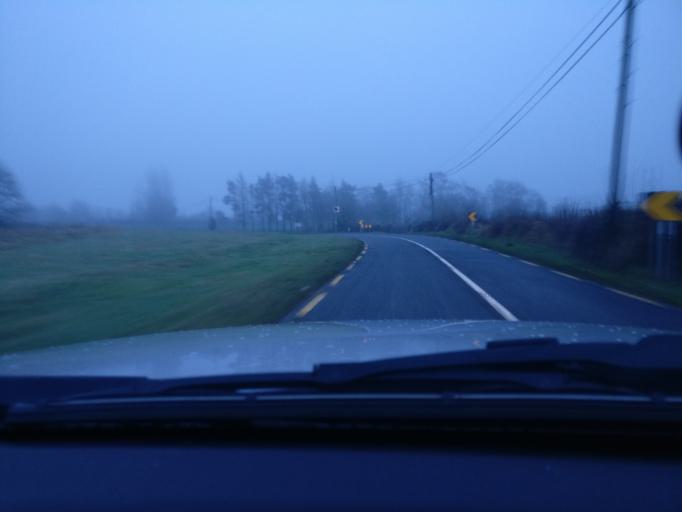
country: IE
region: Leinster
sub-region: An Mhi
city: Athboy
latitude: 53.6085
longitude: -6.9555
